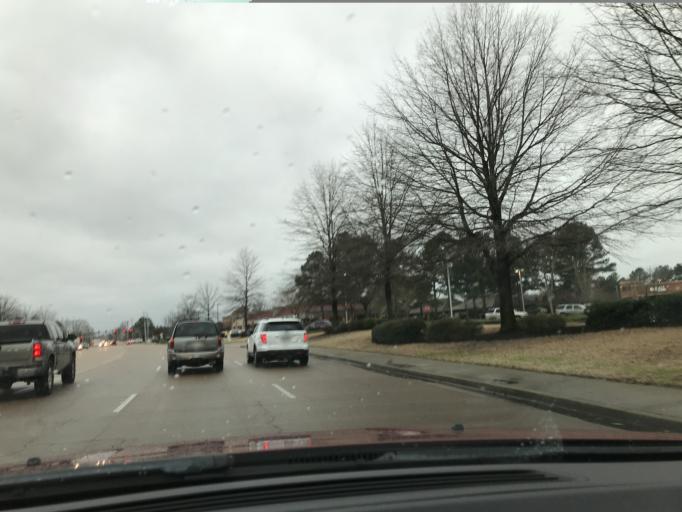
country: US
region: Tennessee
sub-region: Shelby County
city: Collierville
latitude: 35.0488
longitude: -89.6890
